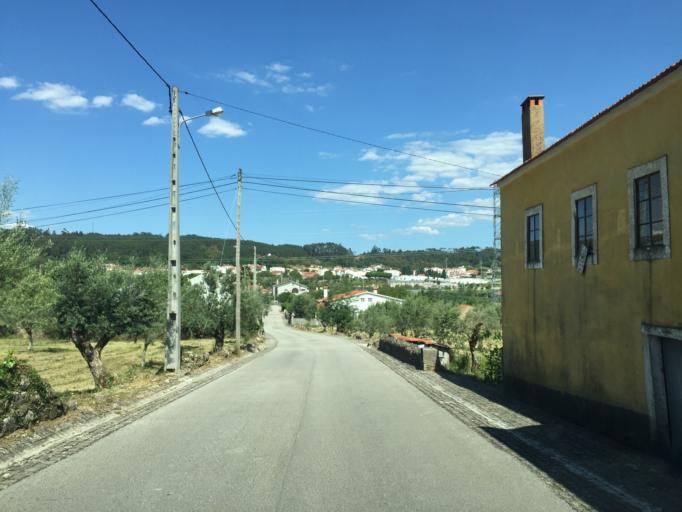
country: PT
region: Leiria
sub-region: Alvaiazere
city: Alvaiazere
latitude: 39.8229
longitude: -8.3931
